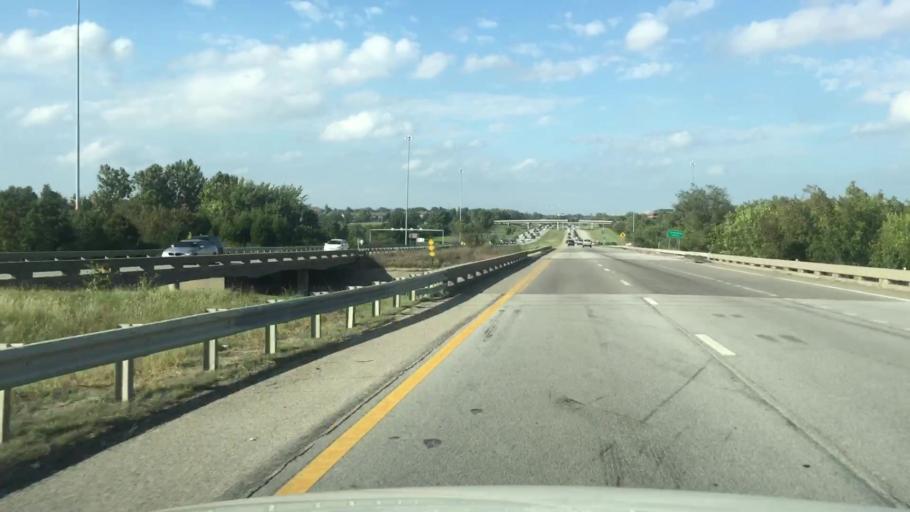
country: US
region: Kansas
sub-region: Johnson County
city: Lenexa
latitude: 38.8835
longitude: -94.6763
